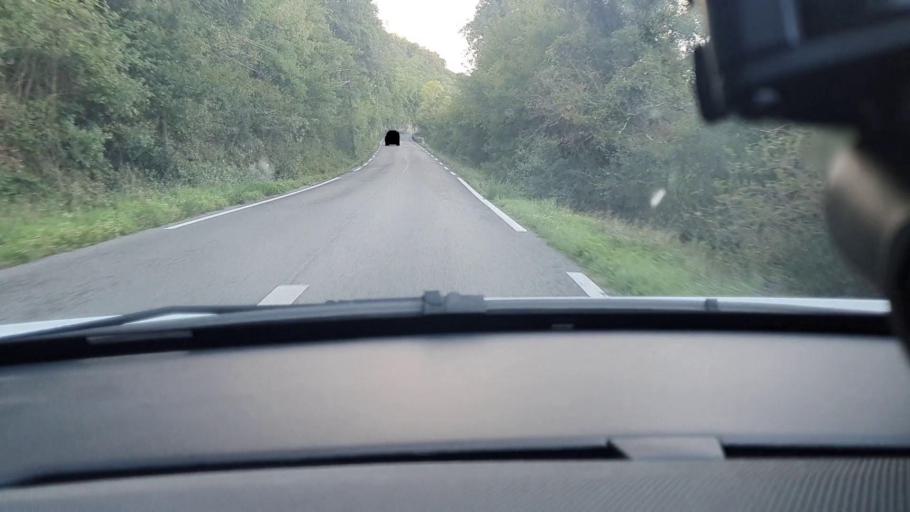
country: FR
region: Languedoc-Roussillon
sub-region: Departement du Gard
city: Barjac
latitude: 44.2429
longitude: 4.2996
